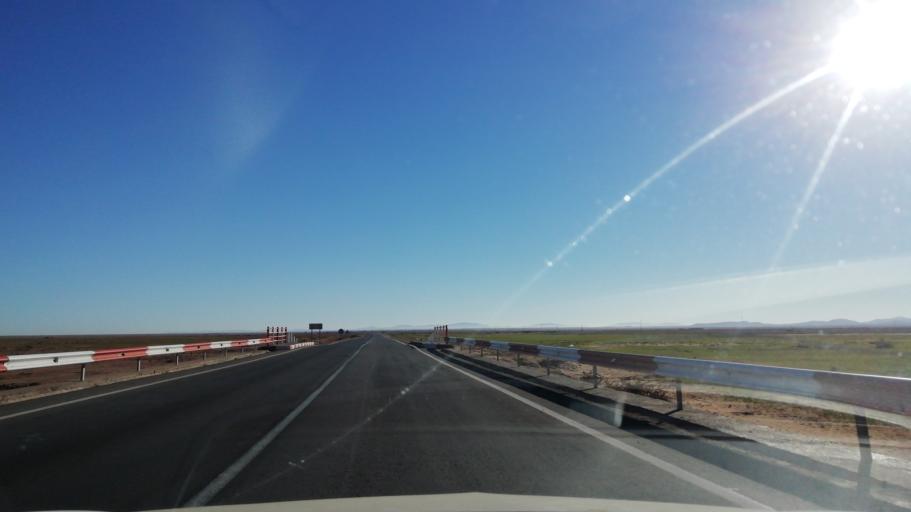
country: DZ
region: El Bayadh
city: El Bayadh
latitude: 33.8591
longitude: 0.5657
